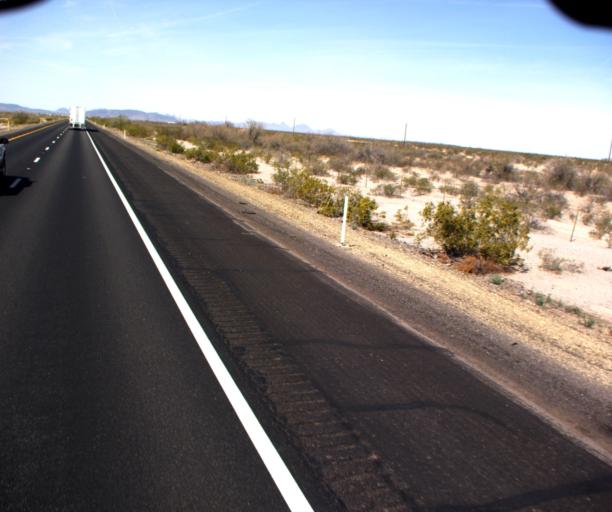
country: US
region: Arizona
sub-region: La Paz County
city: Salome
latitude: 33.6226
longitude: -113.7091
